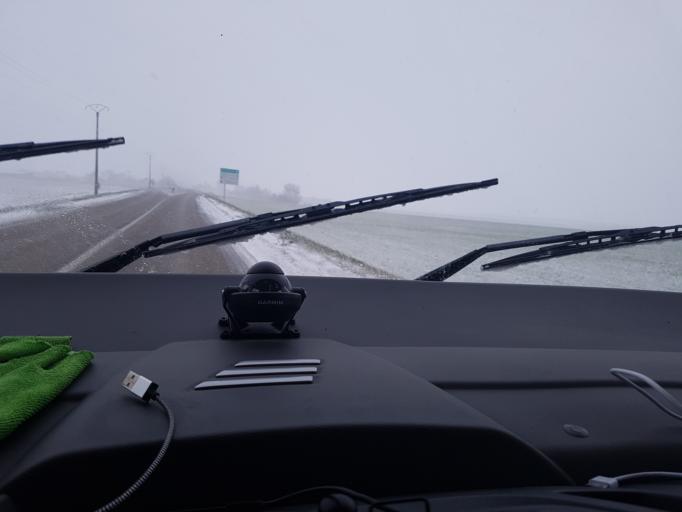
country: FR
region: Lorraine
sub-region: Departement de la Moselle
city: Chateau-Salins
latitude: 48.8680
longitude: 6.4268
